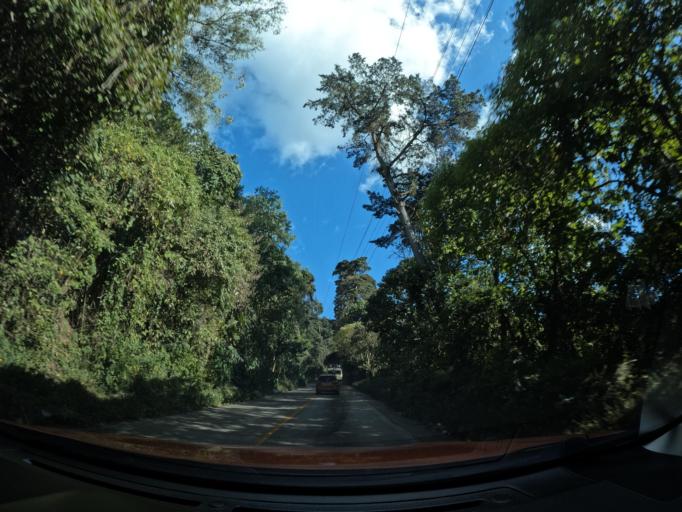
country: GT
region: Sacatepequez
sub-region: Municipio de Santa Maria de Jesus
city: Santa Maria de Jesus
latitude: 14.5072
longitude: -90.7163
